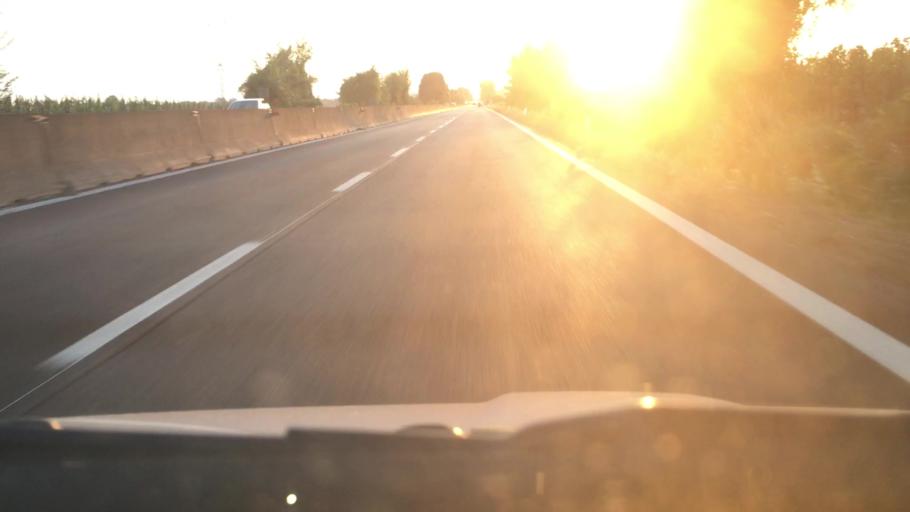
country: IT
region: Emilia-Romagna
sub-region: Provincia di Ferrara
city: Voghiera
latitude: 44.7822
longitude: 11.7622
